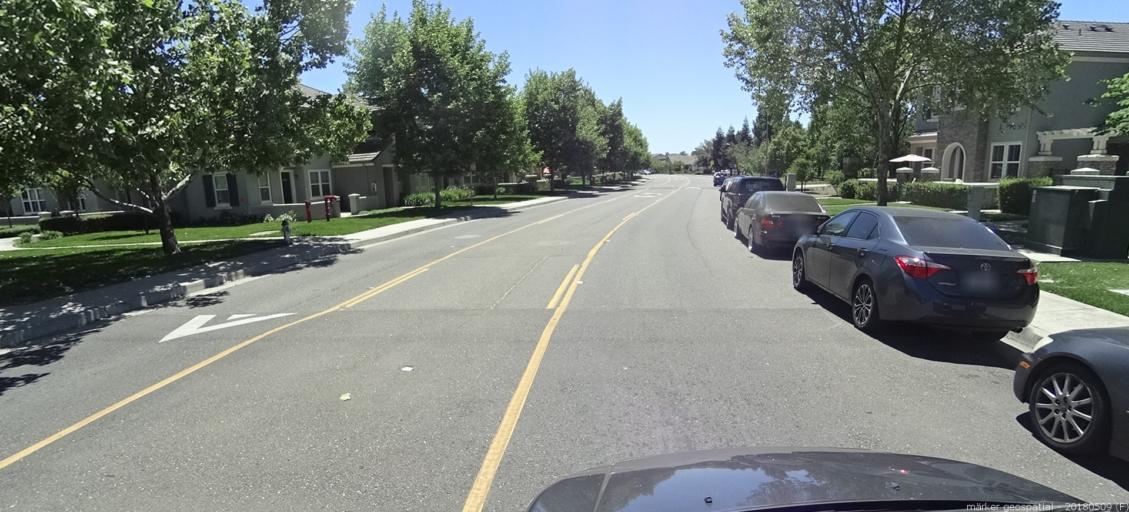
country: US
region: California
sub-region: Sacramento County
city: Sacramento
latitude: 38.6430
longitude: -121.5110
